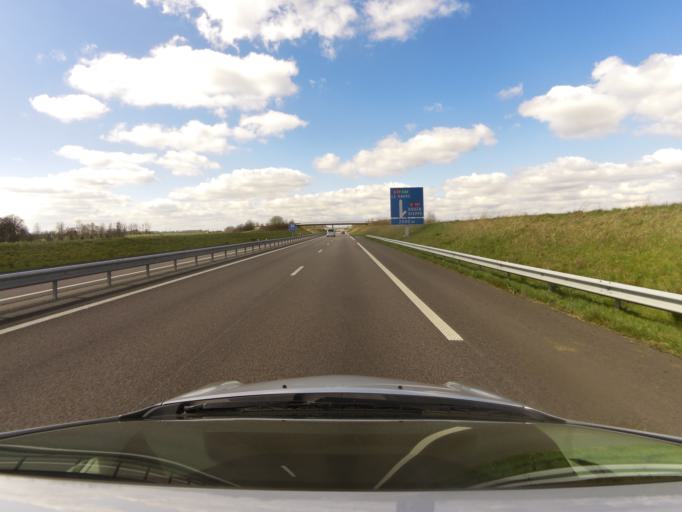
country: FR
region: Haute-Normandie
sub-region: Departement de la Seine-Maritime
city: Cleres
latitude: 49.6376
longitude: 1.0870
